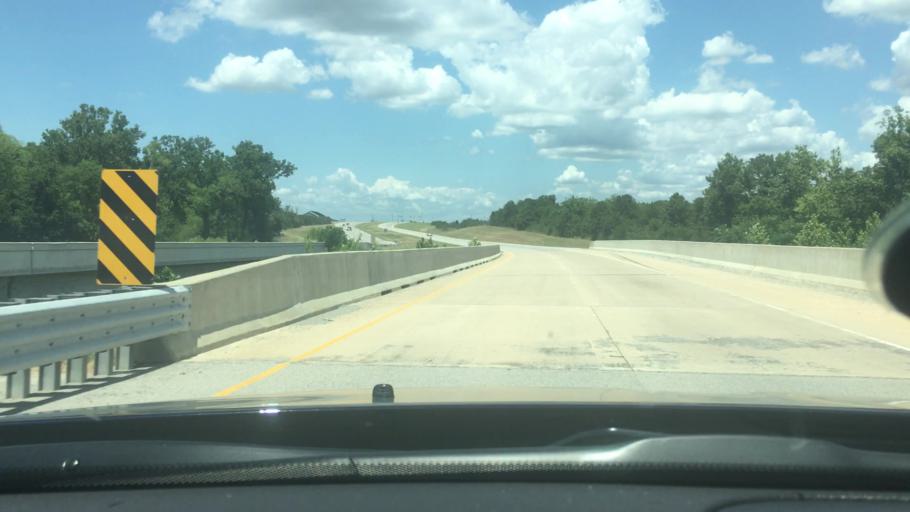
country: US
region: Oklahoma
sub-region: Bryan County
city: Calera
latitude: 33.9892
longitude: -96.4275
